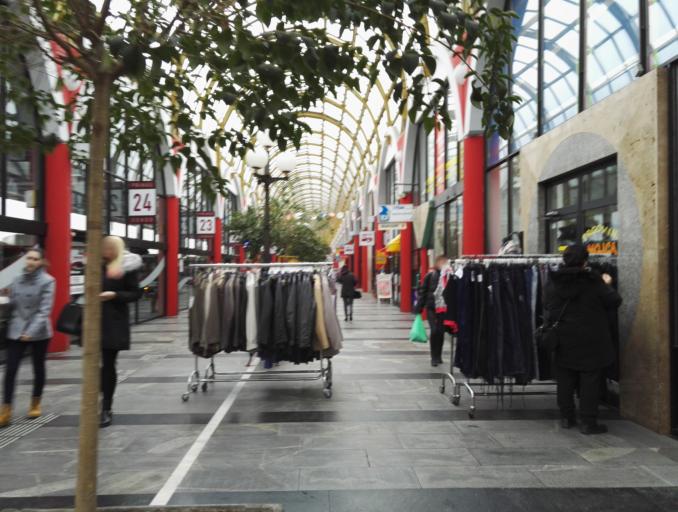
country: SI
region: Maribor
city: Maribor
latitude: 46.5605
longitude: 15.6561
